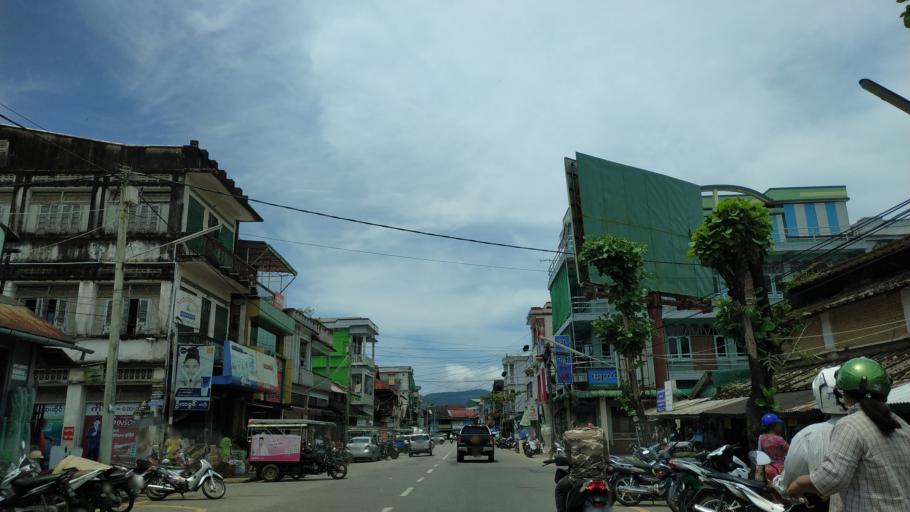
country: MM
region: Tanintharyi
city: Dawei
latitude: 14.0720
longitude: 98.1911
